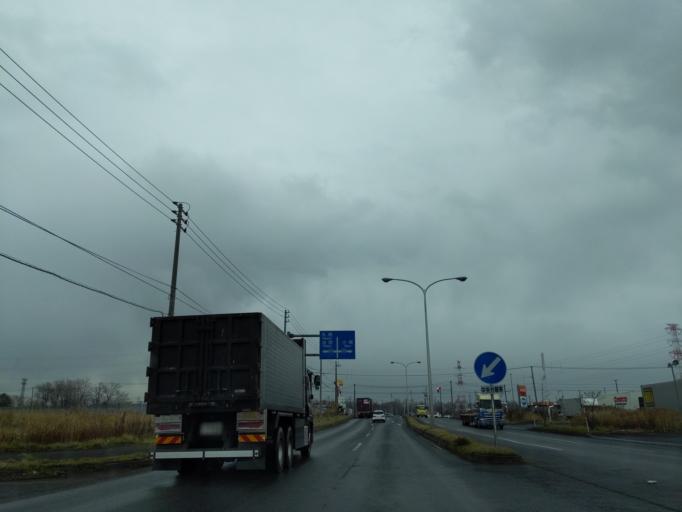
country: JP
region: Hokkaido
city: Ishikari
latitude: 43.1862
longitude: 141.3086
